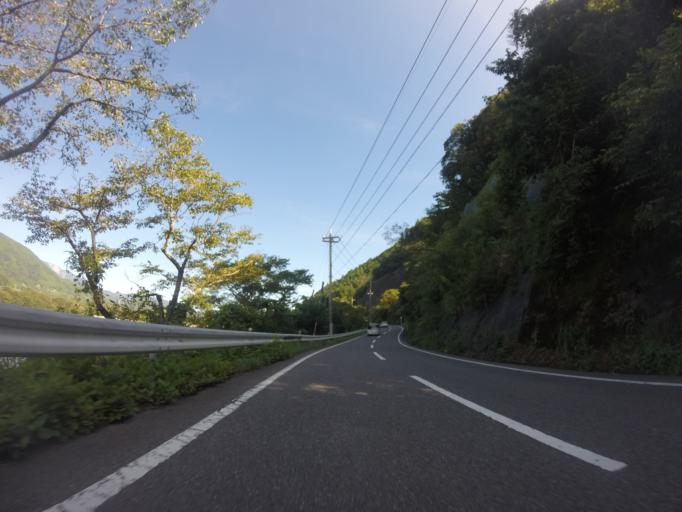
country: JP
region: Shizuoka
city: Fujinomiya
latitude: 35.3031
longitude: 138.4565
